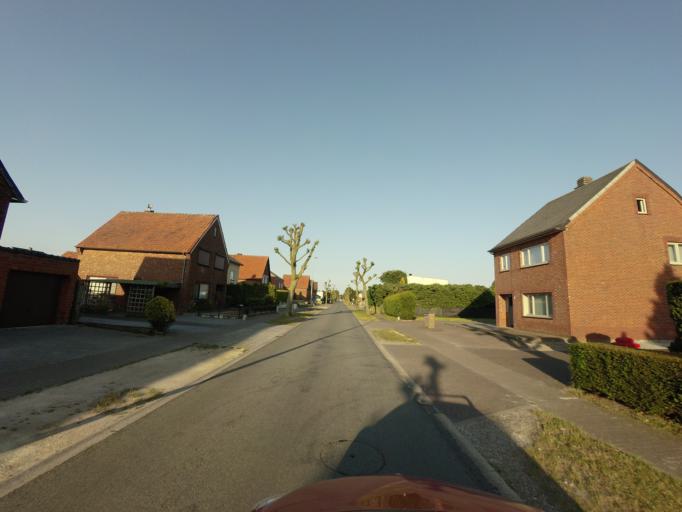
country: BE
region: Flanders
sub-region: Provincie Limburg
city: Lommel
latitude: 51.2363
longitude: 5.3600
